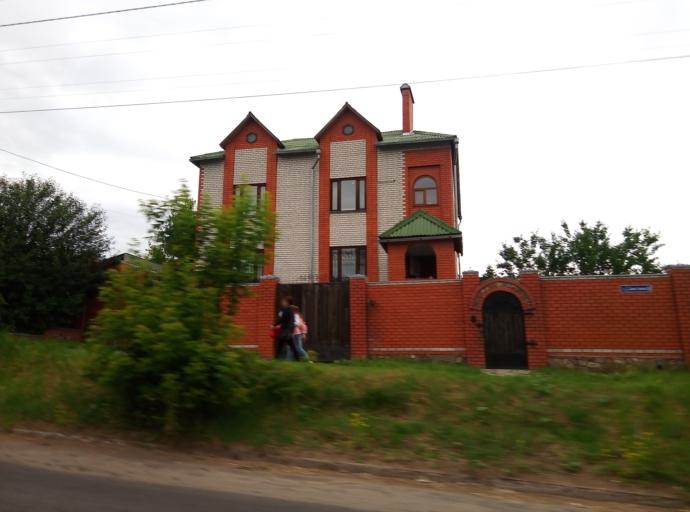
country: RU
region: Kursk
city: Kursk
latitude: 51.7327
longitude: 36.1600
